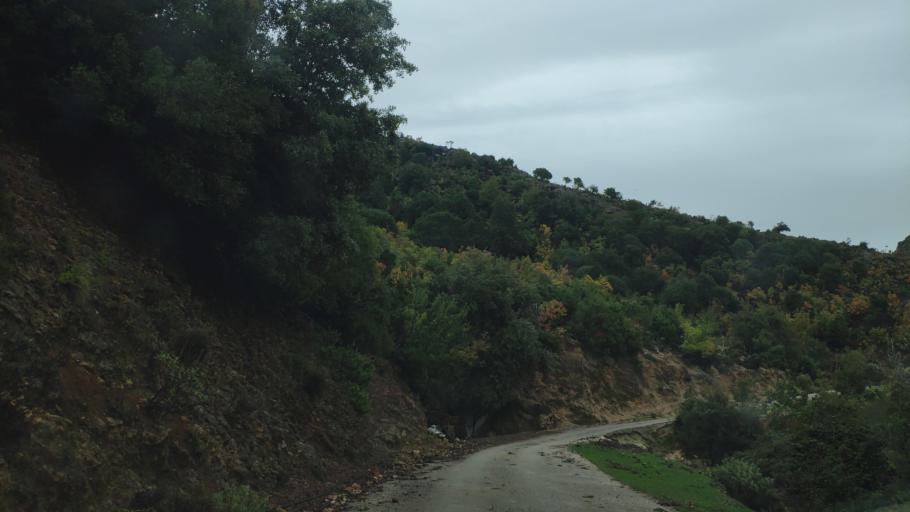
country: GR
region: Epirus
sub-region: Nomos Prevezis
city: Kanalaki
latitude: 39.3424
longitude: 20.6524
